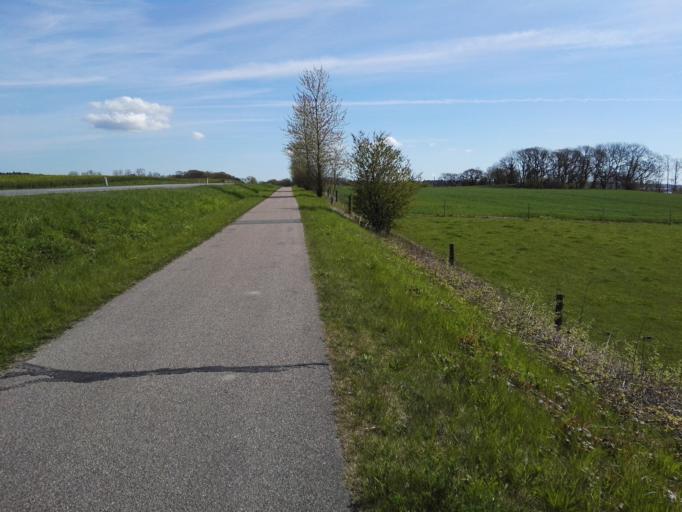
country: DK
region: Capital Region
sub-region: Halsnaes Kommune
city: Liseleje
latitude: 55.9644
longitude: 11.9601
